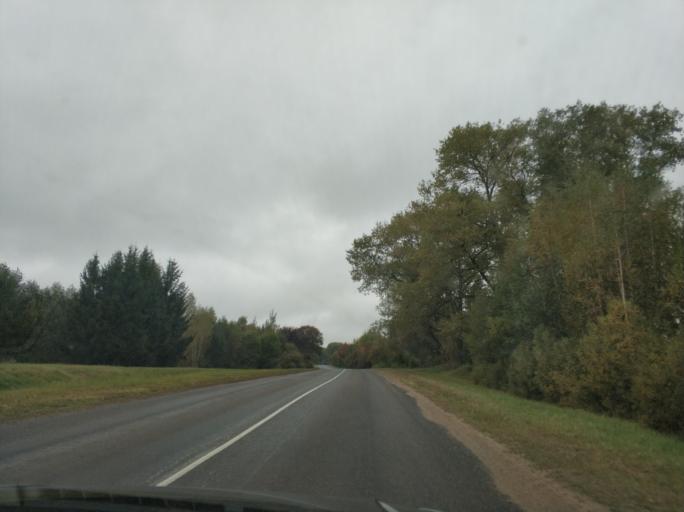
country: BY
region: Vitebsk
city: Polatsk
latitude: 55.4428
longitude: 28.9508
